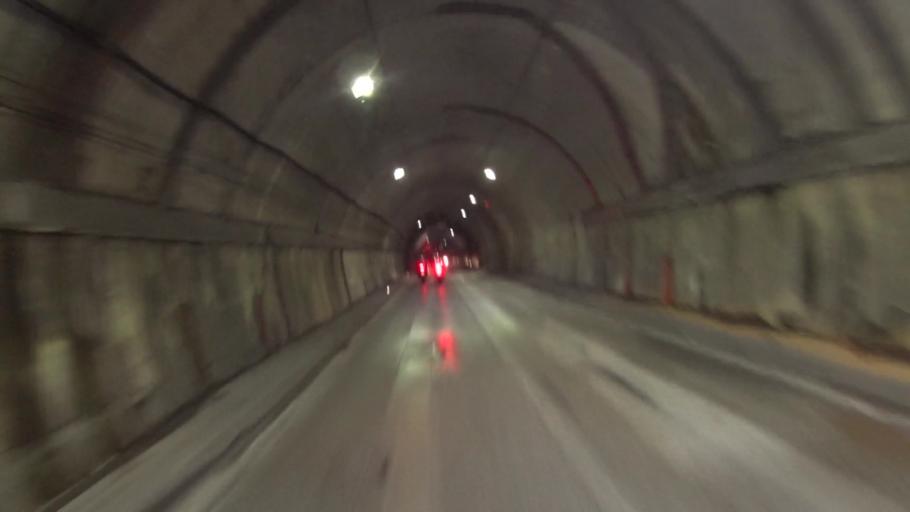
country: JP
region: Shiga Prefecture
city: Kitahama
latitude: 35.1899
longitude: 135.8563
